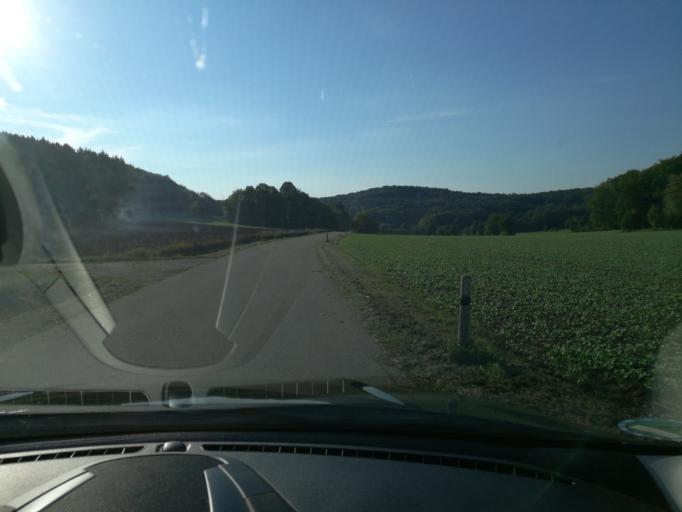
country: DE
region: Bavaria
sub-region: Upper Palatinate
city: Parsberg
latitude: 49.1884
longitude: 11.7237
